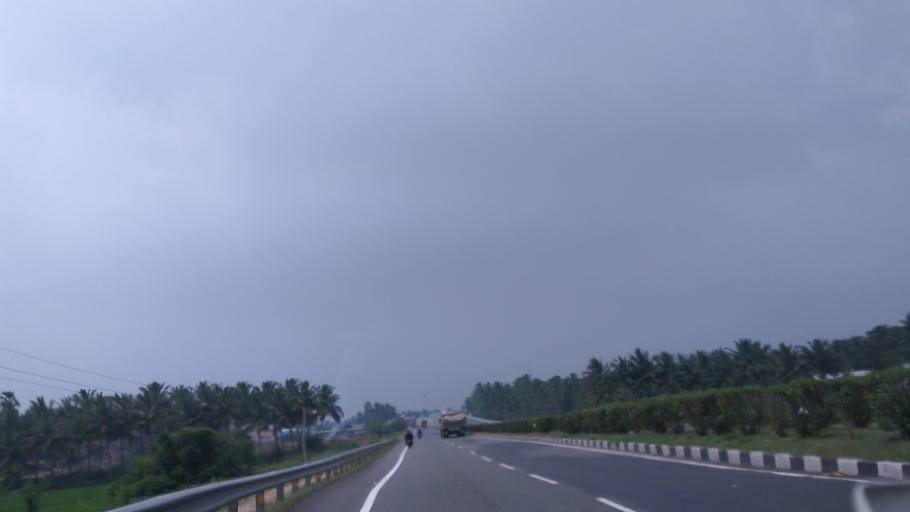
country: IN
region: Tamil Nadu
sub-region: Krishnagiri
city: Kaverippattanam
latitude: 12.4051
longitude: 78.2222
